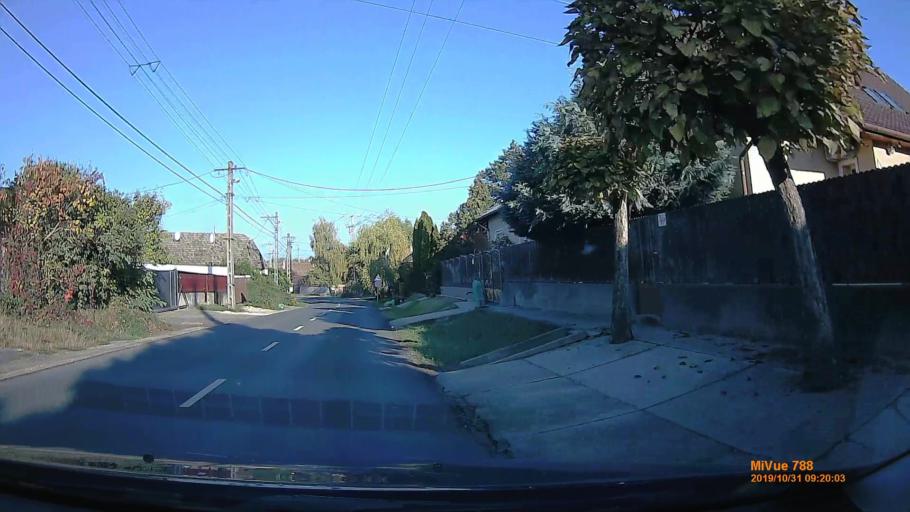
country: HU
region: Pest
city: Gyomro
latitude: 47.4212
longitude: 19.3877
